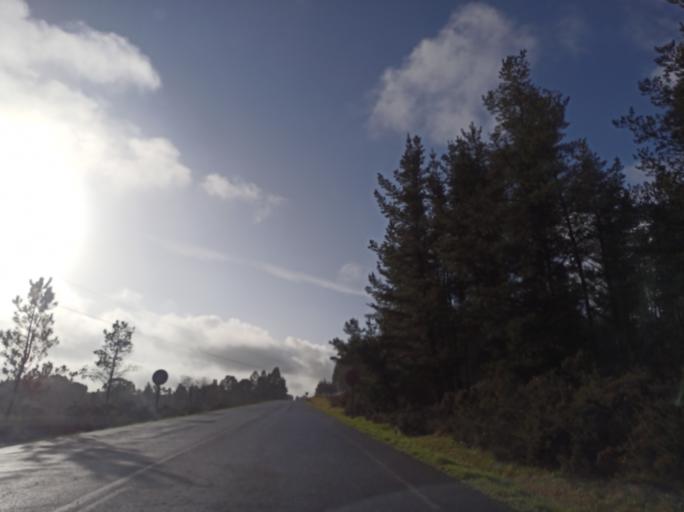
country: ES
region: Galicia
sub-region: Provincia da Coruna
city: Curtis
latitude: 43.1216
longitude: -8.0295
